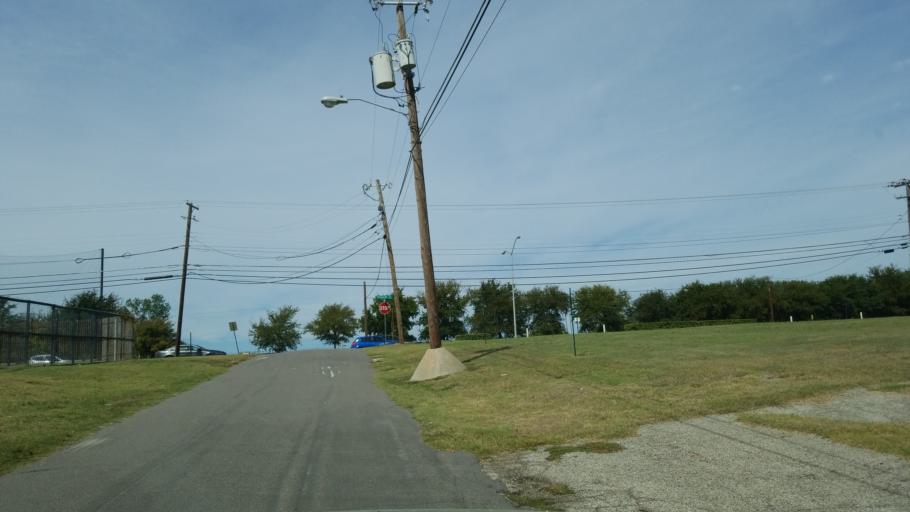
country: US
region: Texas
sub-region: Dallas County
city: Highland Park
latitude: 32.7970
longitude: -96.7187
